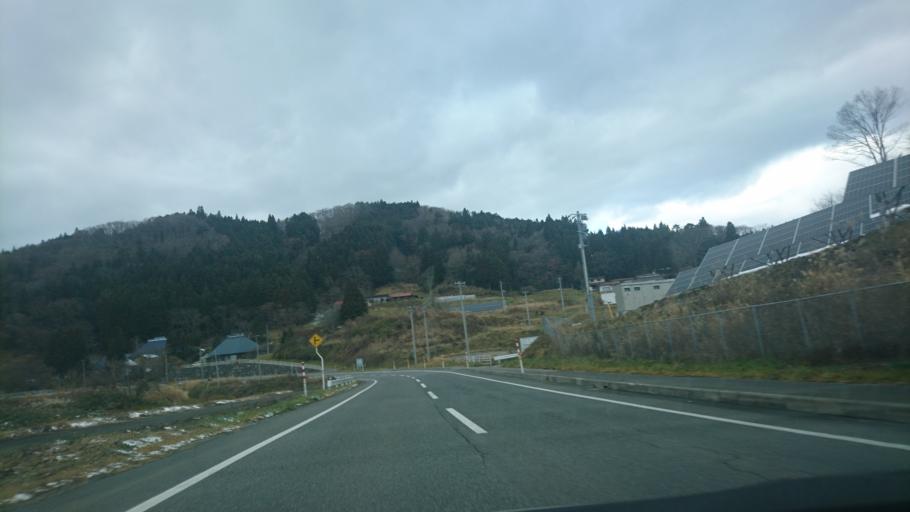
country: JP
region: Iwate
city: Mizusawa
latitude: 39.1819
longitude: 141.2943
